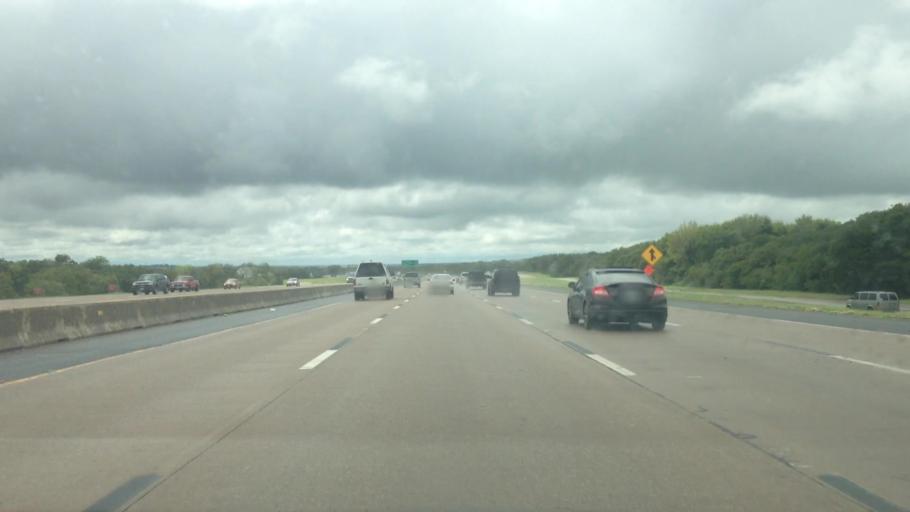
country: US
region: Texas
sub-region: Tarrant County
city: Lake Worth
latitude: 32.7982
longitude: -97.4415
